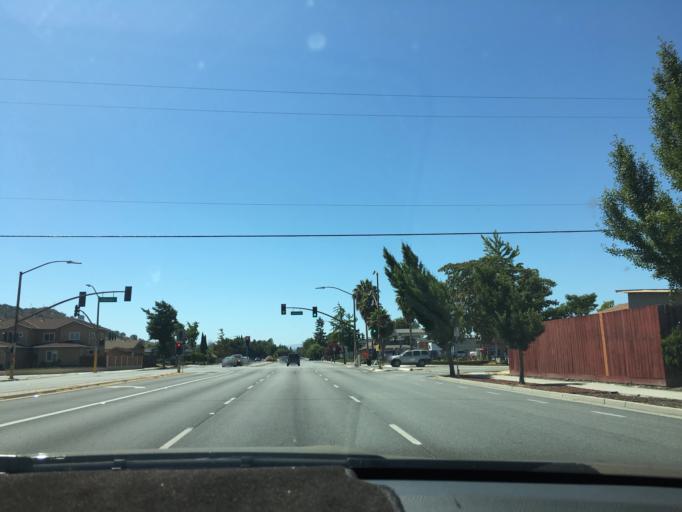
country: US
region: California
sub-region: Santa Clara County
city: Seven Trees
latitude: 37.2387
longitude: -121.8499
